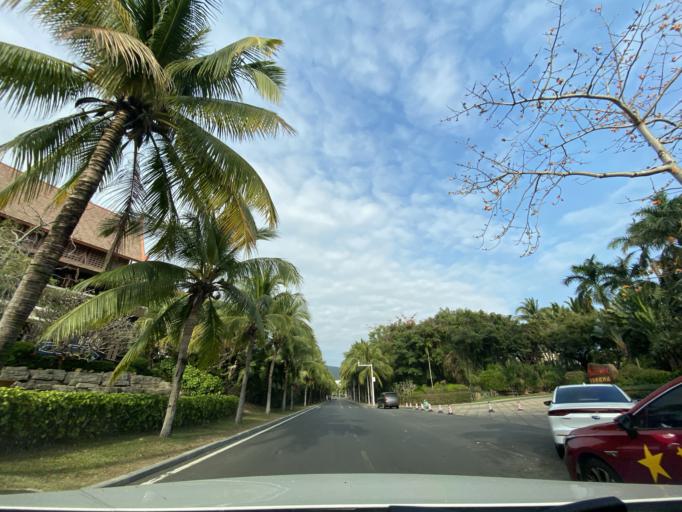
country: CN
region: Hainan
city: Tiandu
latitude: 18.2295
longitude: 109.6250
